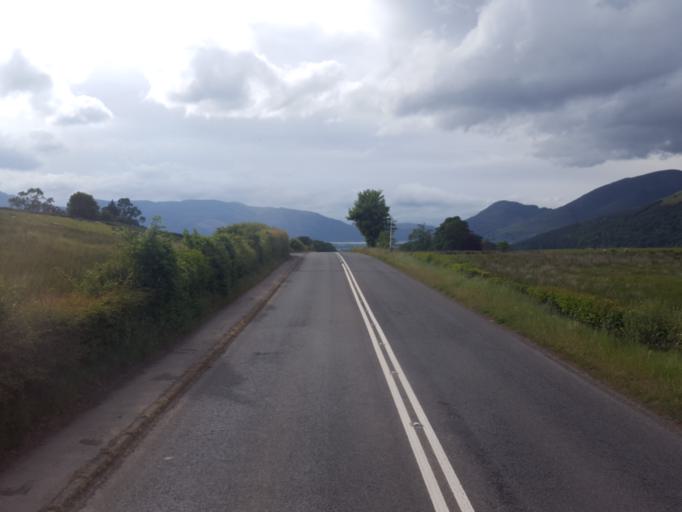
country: GB
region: England
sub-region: Cumbria
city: Keswick
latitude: 54.5953
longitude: -3.1053
